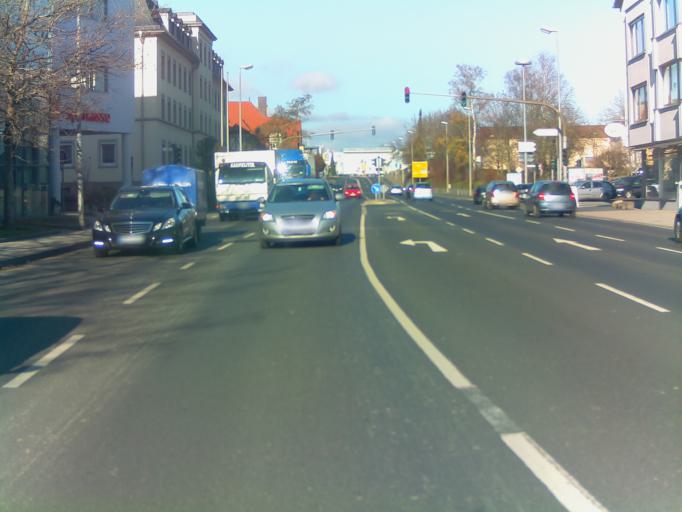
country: DE
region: Bavaria
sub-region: Regierungsbezirk Unterfranken
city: Bad Neustadt an der Saale
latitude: 50.3270
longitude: 10.2207
